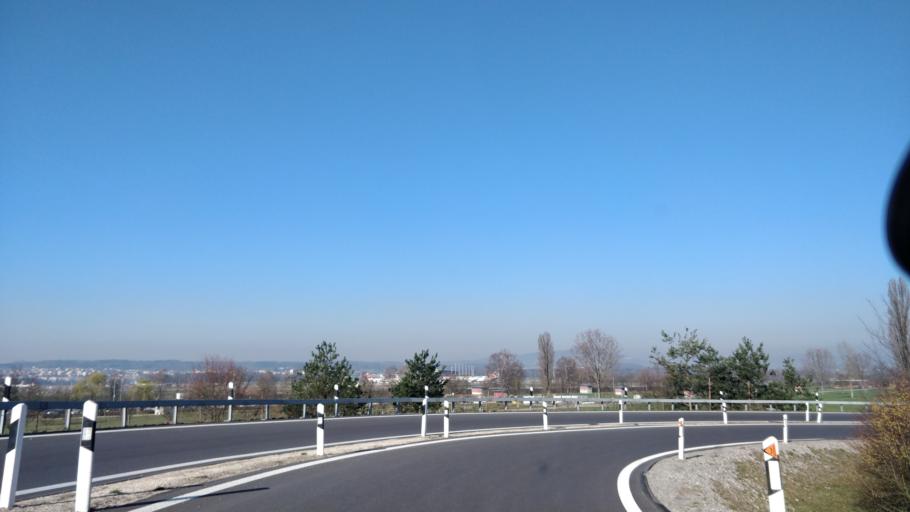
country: CH
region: Zurich
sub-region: Bezirk Buelach
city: Kloten / Freienberg (Chanzler-Chlini Chaseren)
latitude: 47.4613
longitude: 8.5745
